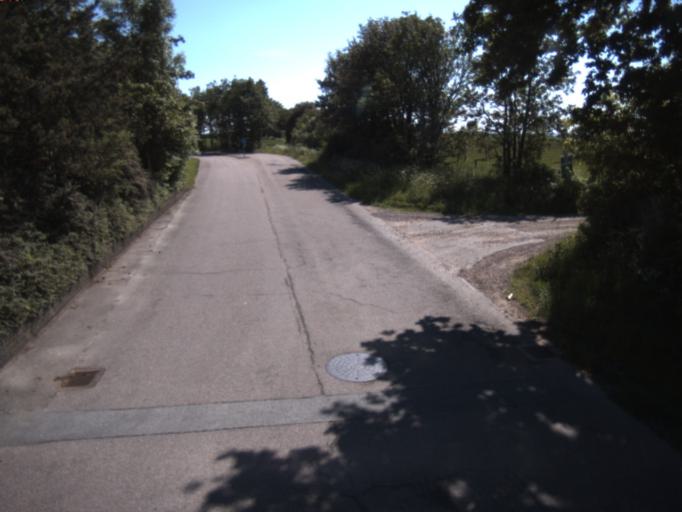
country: SE
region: Skane
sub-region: Helsingborg
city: Gantofta
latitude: 55.9862
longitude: 12.7940
